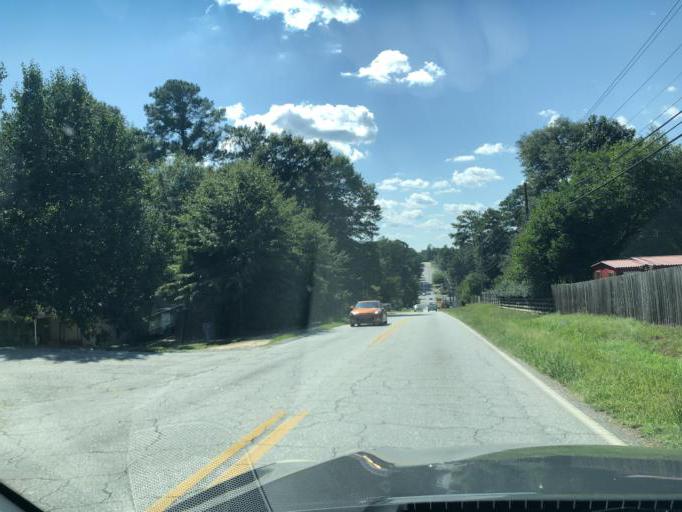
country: US
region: Georgia
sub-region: Muscogee County
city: Columbus
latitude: 32.5397
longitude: -84.9303
